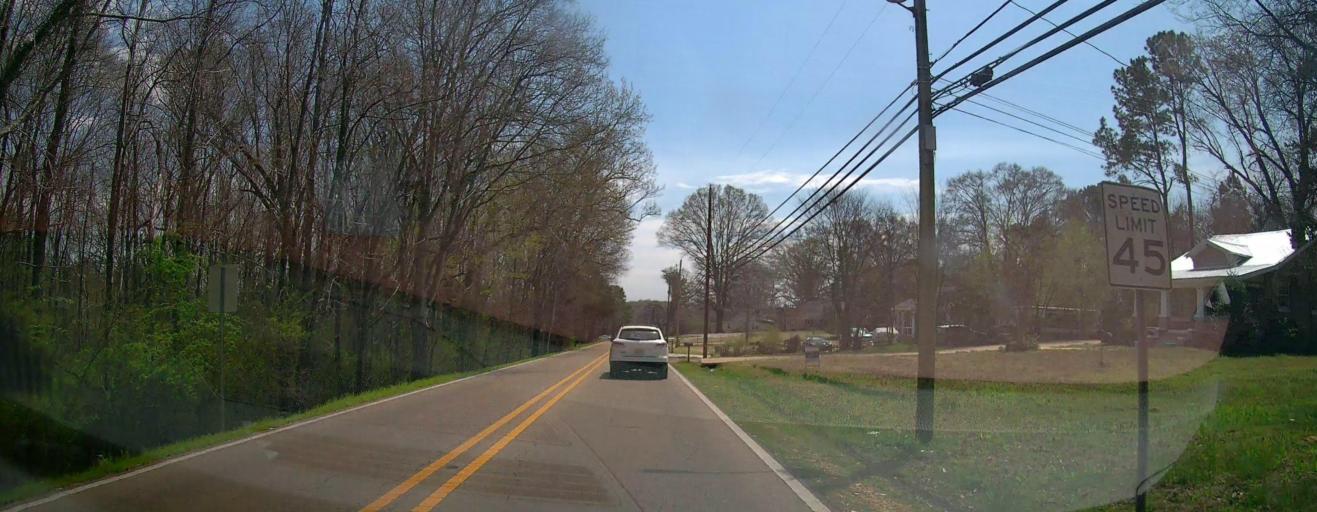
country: US
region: Mississippi
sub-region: Union County
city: New Albany
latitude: 34.4775
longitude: -88.9975
